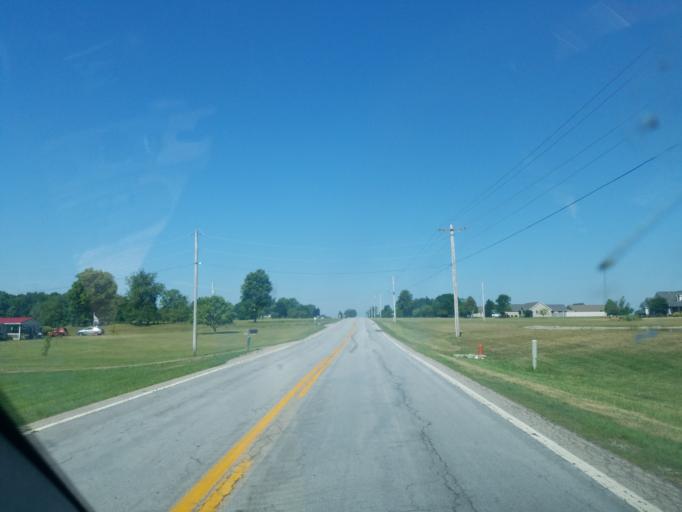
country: US
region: Ohio
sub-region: Logan County
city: Northwood
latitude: 40.4379
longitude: -83.7850
